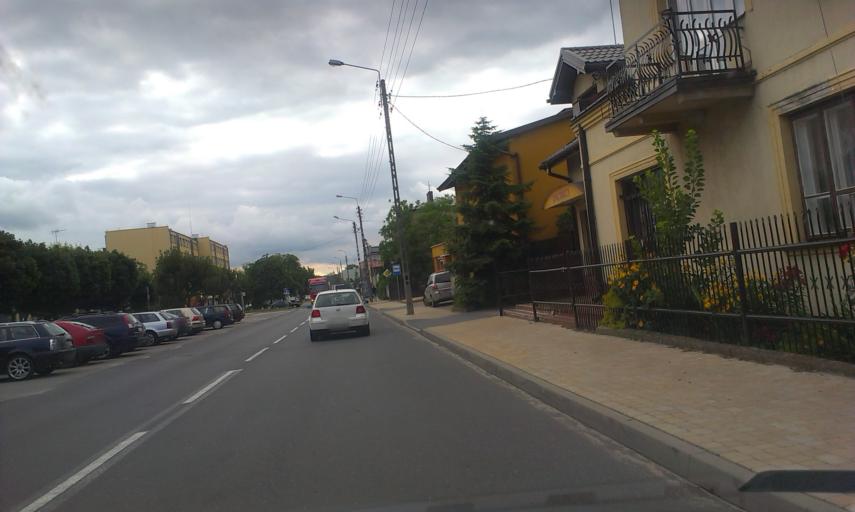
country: PL
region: Masovian Voivodeship
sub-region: Powiat zyrardowski
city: Mszczonow
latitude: 51.9741
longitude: 20.5225
